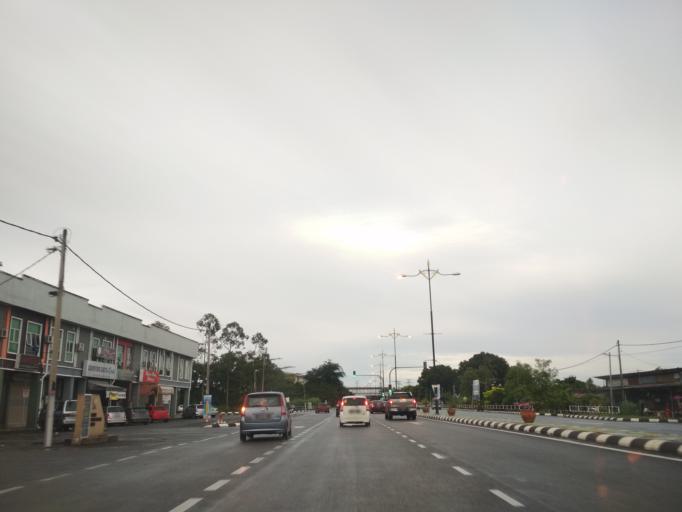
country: MY
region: Perlis
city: Kangar
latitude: 6.4360
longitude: 100.2043
